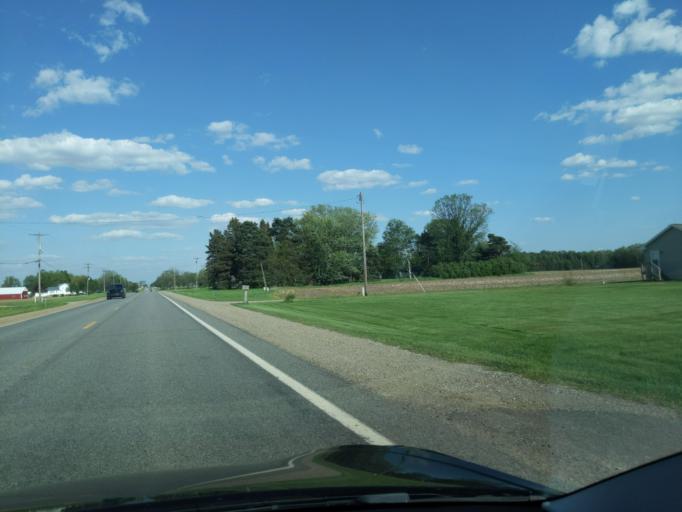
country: US
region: Michigan
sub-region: Ionia County
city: Portland
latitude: 42.7556
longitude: -84.9132
